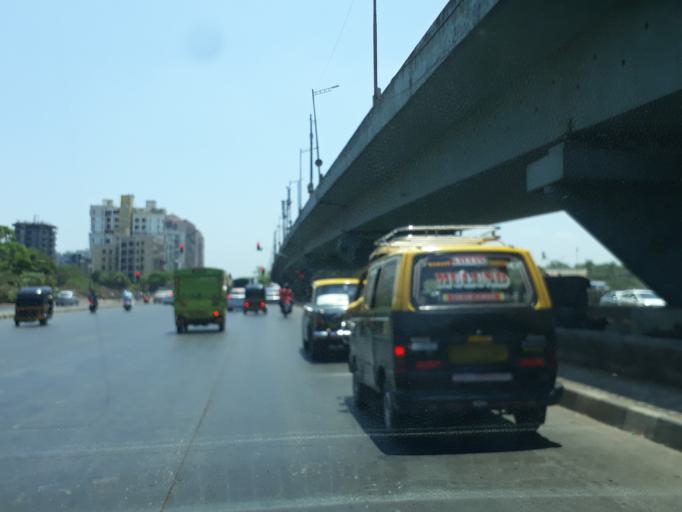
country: IN
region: Maharashtra
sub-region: Mumbai Suburban
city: Mumbai
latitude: 19.0702
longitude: 72.9062
